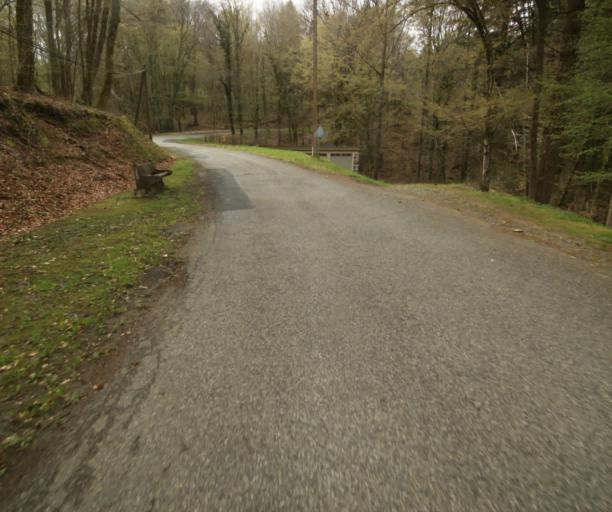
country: FR
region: Limousin
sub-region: Departement de la Correze
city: Argentat
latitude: 45.1975
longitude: 1.9683
